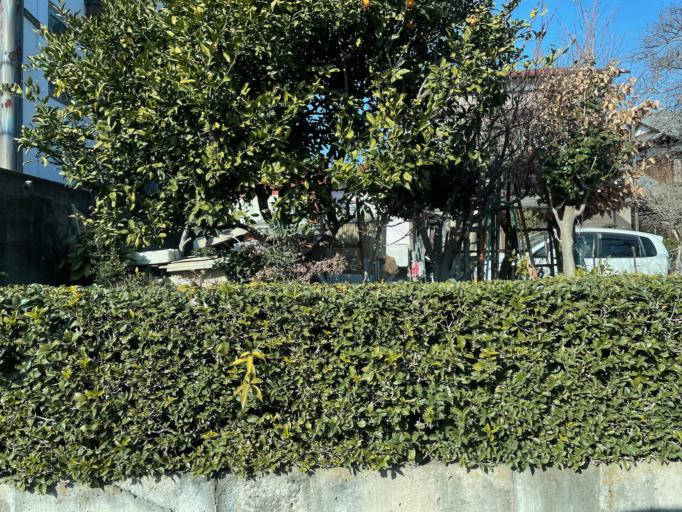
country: JP
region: Tokyo
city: Kokubunji
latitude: 35.7309
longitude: 139.4915
